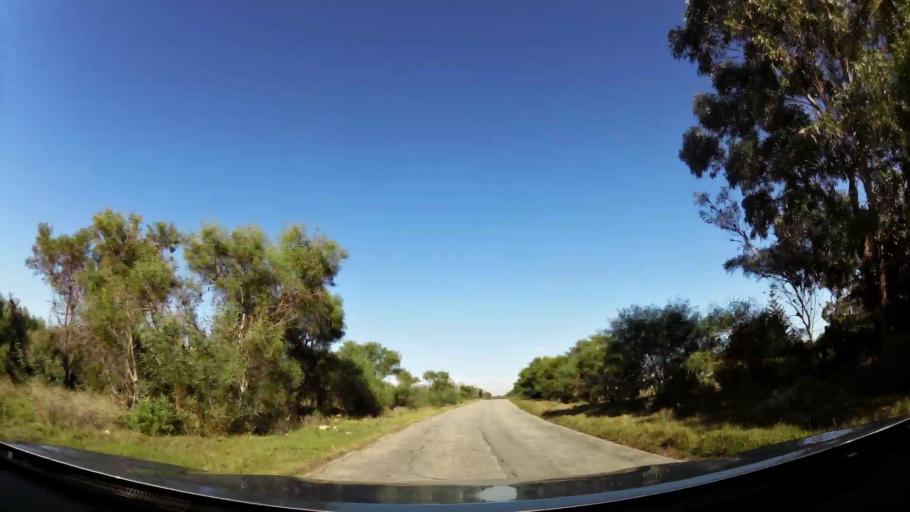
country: ZA
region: Eastern Cape
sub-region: Nelson Mandela Bay Metropolitan Municipality
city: Port Elizabeth
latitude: -33.9878
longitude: 25.6324
